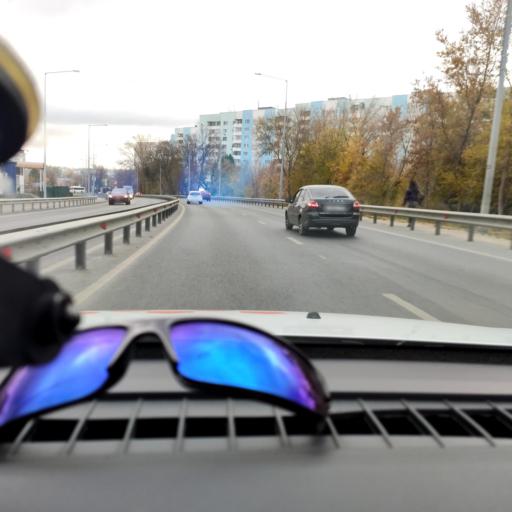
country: RU
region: Samara
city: Volzhskiy
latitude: 53.3526
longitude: 50.2125
